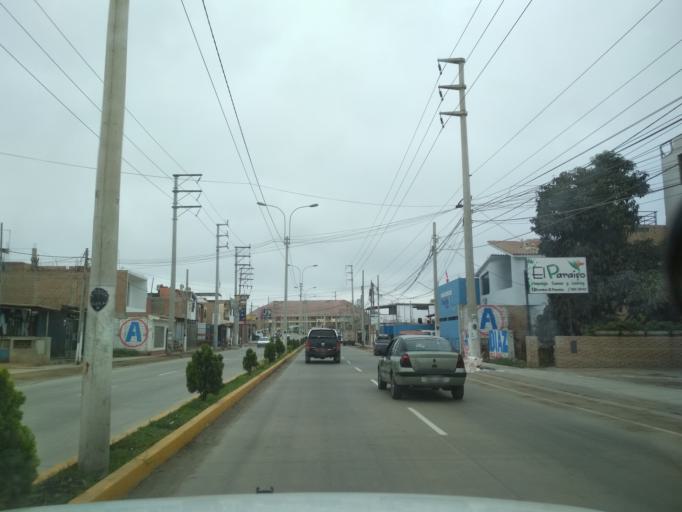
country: PE
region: Lima
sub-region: Provincia de Canete
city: San Vicente de Canete
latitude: -13.0745
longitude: -76.3721
